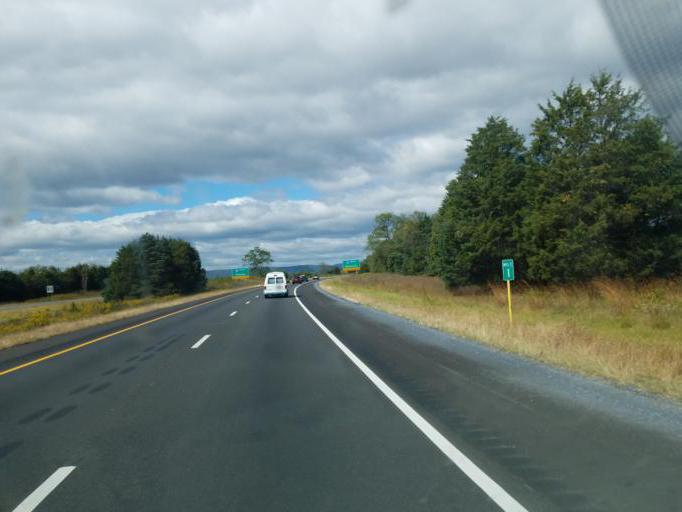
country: US
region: Virginia
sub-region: Frederick County
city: Middletown
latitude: 39.0020
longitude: -78.2852
